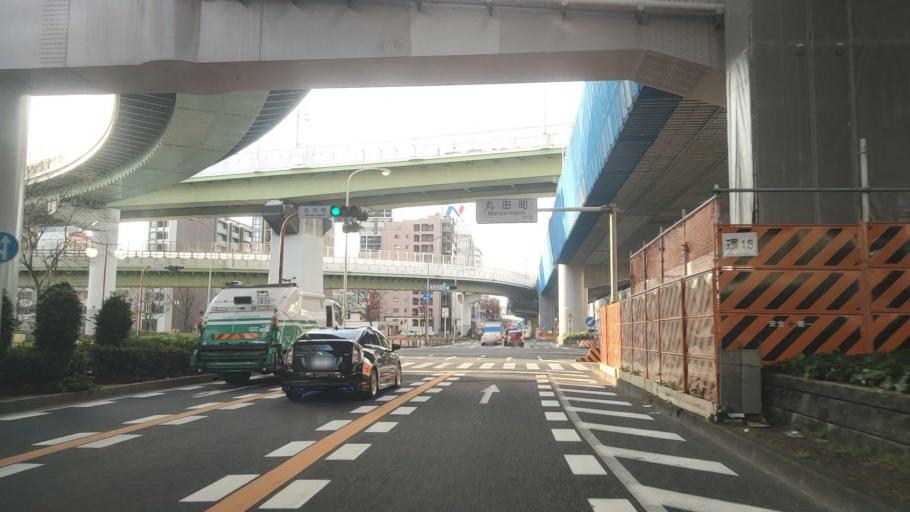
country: JP
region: Aichi
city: Nagoya-shi
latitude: 35.1621
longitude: 136.9156
